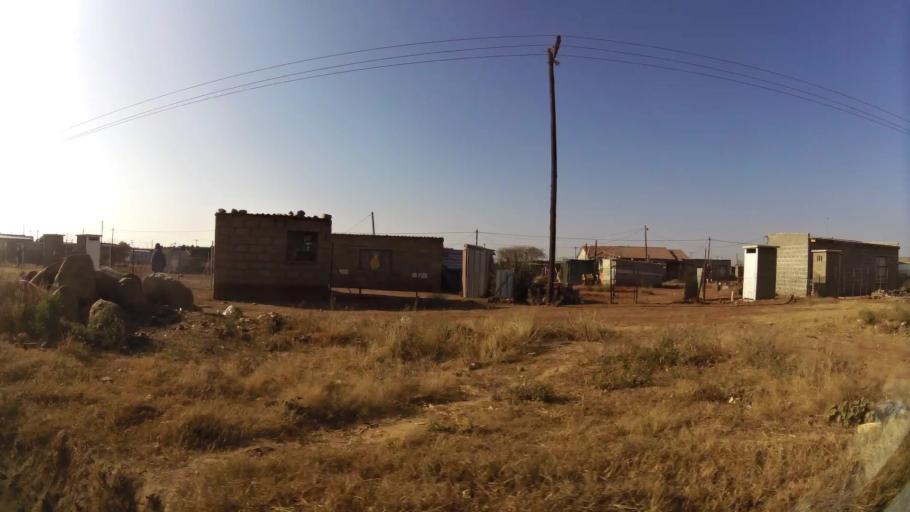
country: ZA
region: Orange Free State
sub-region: Mangaung Metropolitan Municipality
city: Bloemfontein
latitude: -29.2042
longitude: 26.2517
